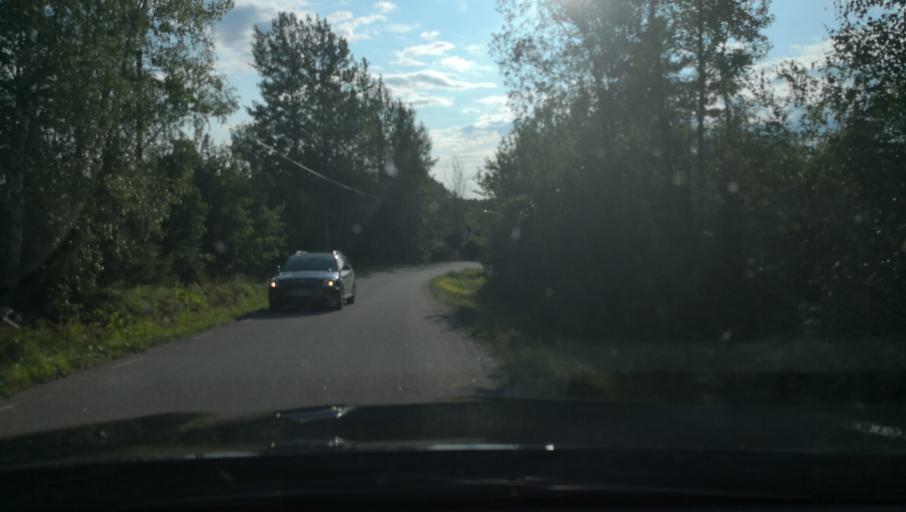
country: SE
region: Uppsala
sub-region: Osthammars Kommun
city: Osterbybruk
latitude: 60.0174
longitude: 17.9266
